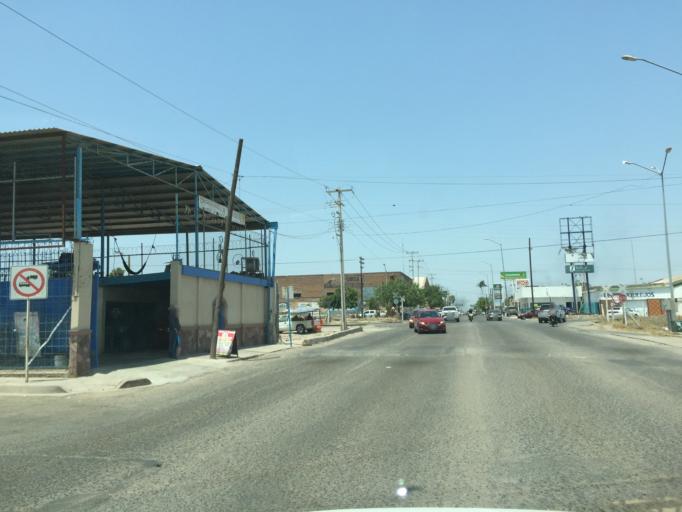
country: MX
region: Sonora
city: Navojoa
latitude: 27.0732
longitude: -109.4399
